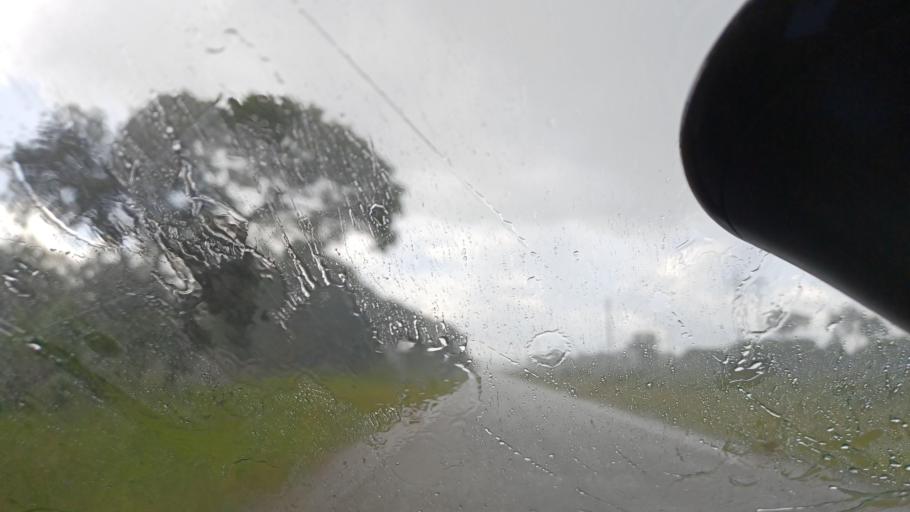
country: ZM
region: North-Western
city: Kasempa
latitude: -13.0965
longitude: 25.9094
